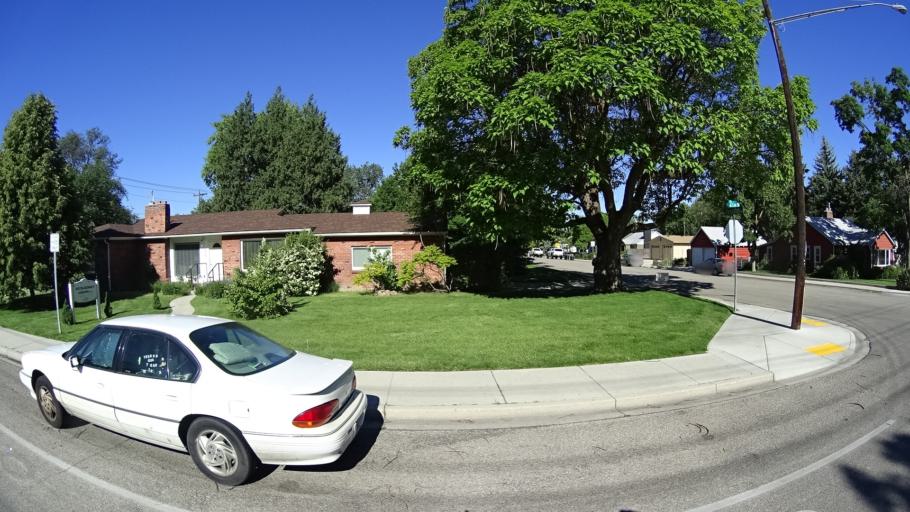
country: US
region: Idaho
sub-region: Ada County
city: Garden City
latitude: 43.6262
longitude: -116.2240
